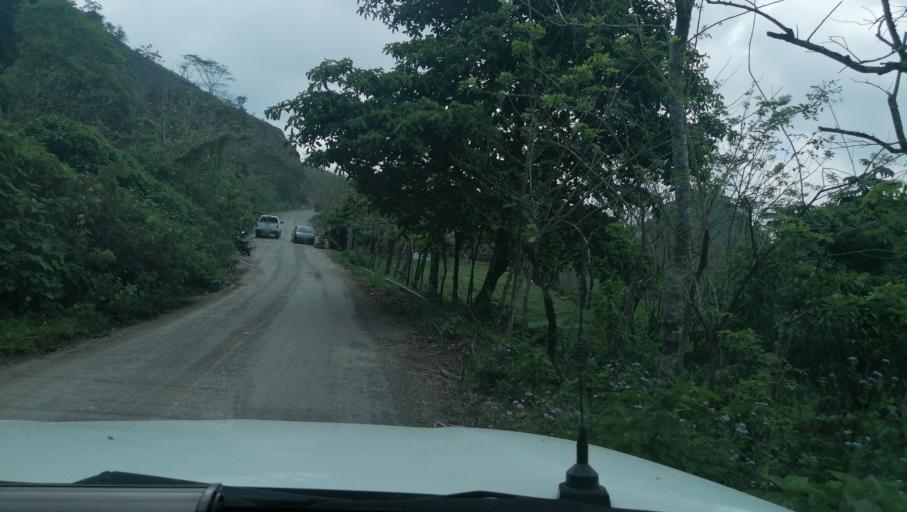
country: MX
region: Chiapas
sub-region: Francisco Leon
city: San Miguel la Sardina
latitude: 17.2455
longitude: -93.2887
